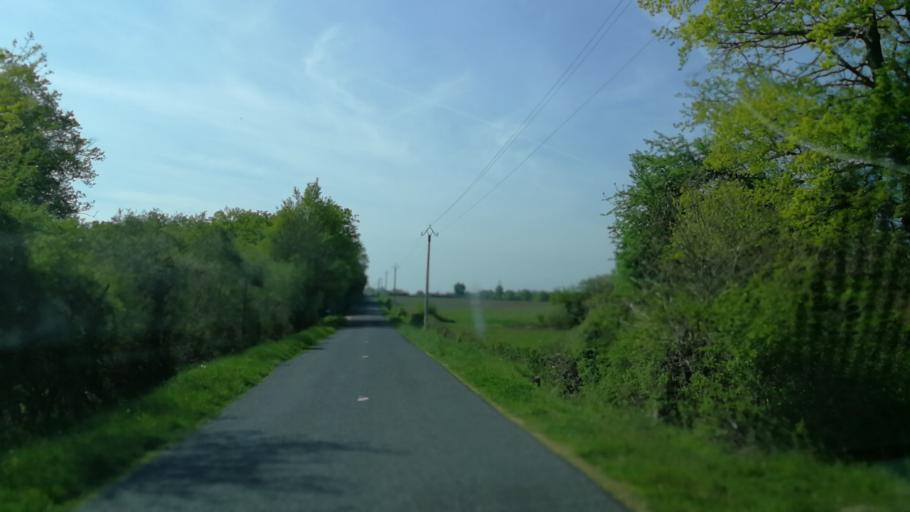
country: FR
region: Auvergne
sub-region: Departement de l'Allier
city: Neuilly-le-Real
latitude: 46.4956
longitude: 3.5110
